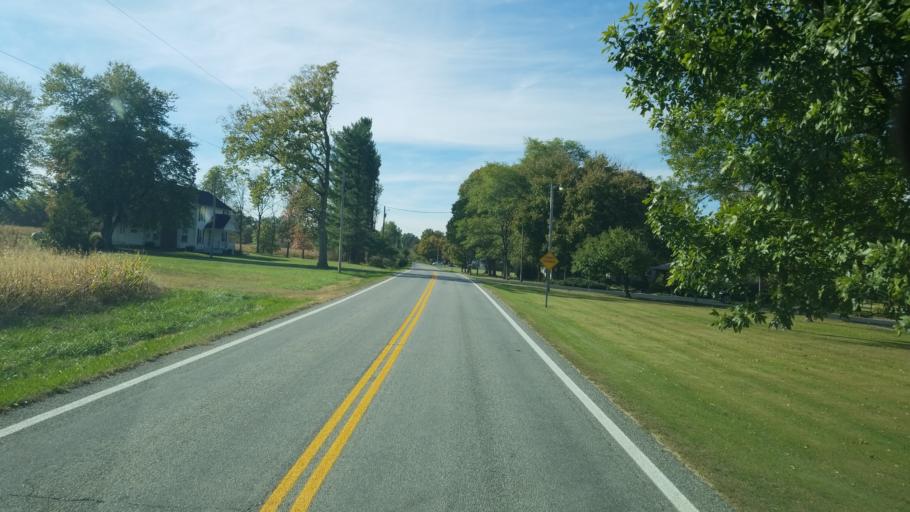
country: US
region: Ohio
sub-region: Warren County
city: Morrow
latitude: 39.4062
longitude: -84.0550
